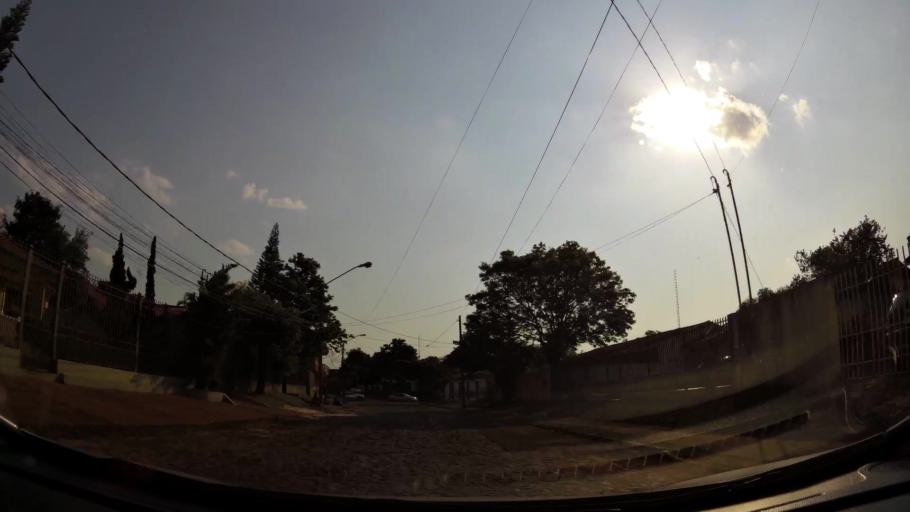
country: PY
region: Alto Parana
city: Presidente Franco
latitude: -25.5341
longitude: -54.6310
